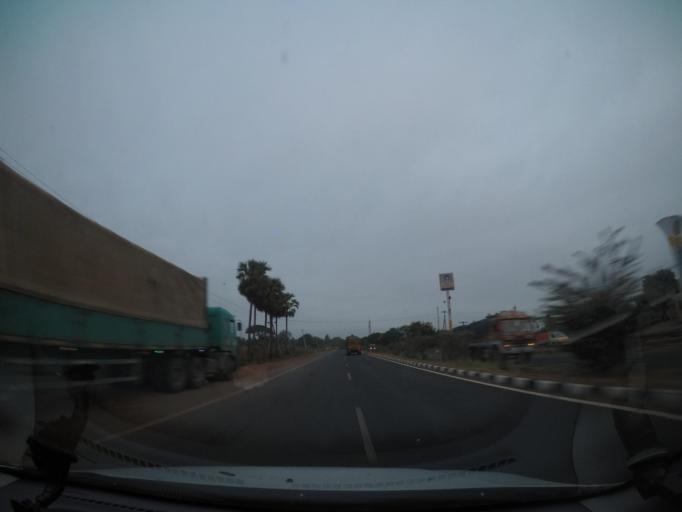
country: IN
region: Andhra Pradesh
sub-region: West Godavari
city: Akividu
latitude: 16.8056
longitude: 81.3069
